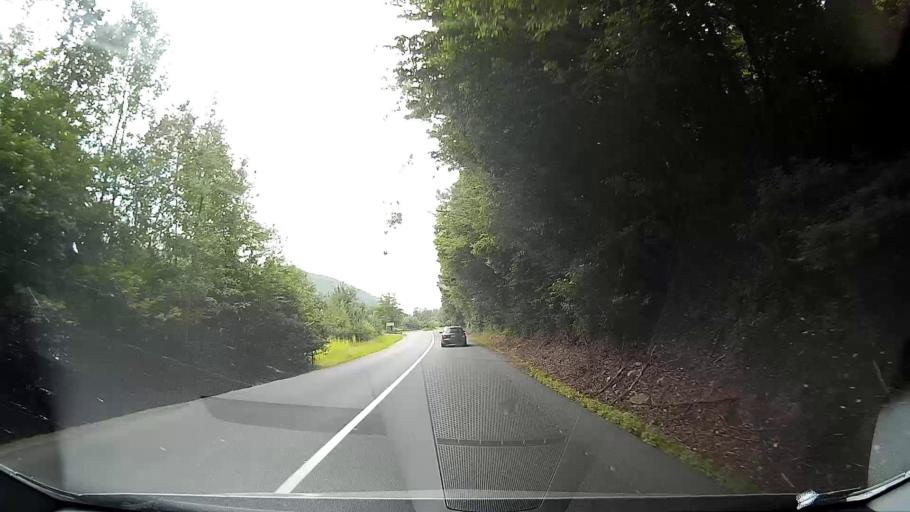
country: SK
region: Banskobystricky
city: Tisovec
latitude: 48.6081
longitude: 19.9558
